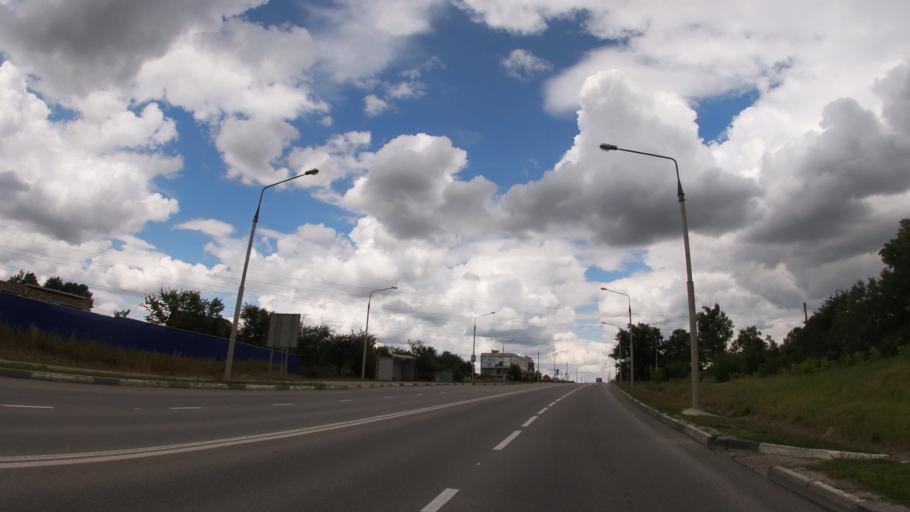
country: RU
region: Belgorod
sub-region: Belgorodskiy Rayon
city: Belgorod
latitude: 50.6250
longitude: 36.6115
